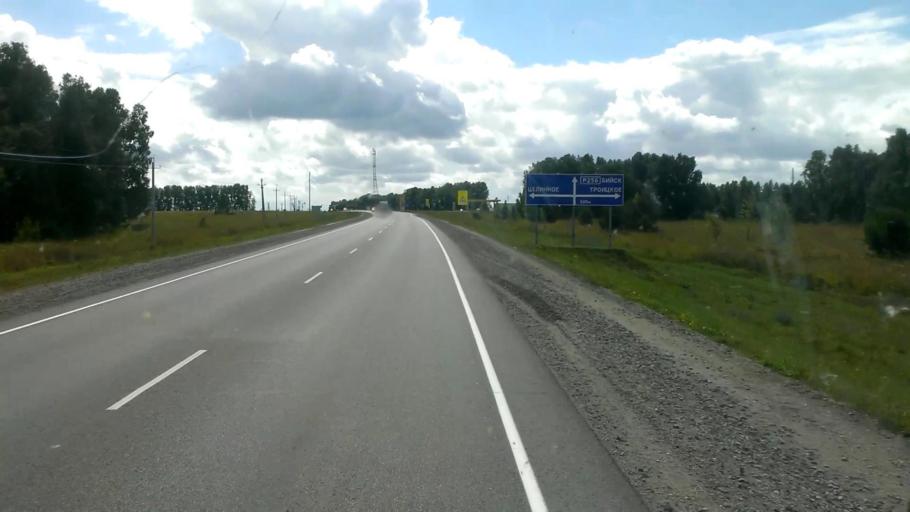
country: RU
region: Altai Krai
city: Troitskoye
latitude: 52.9717
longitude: 84.7481
